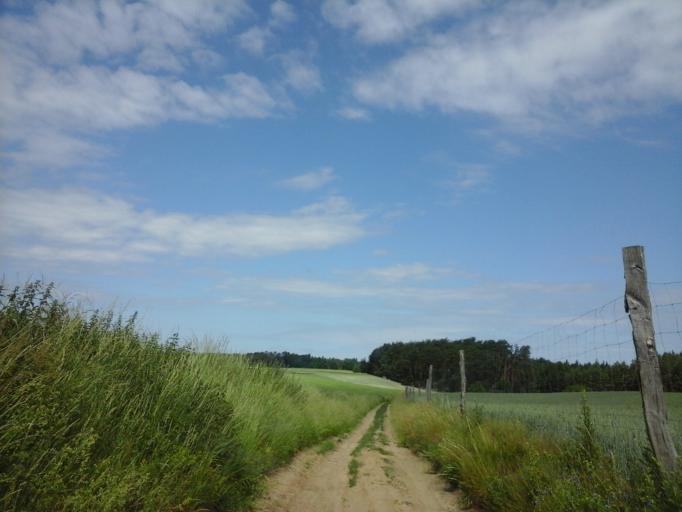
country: PL
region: West Pomeranian Voivodeship
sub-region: Powiat choszczenski
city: Choszczno
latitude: 53.2301
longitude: 15.4268
